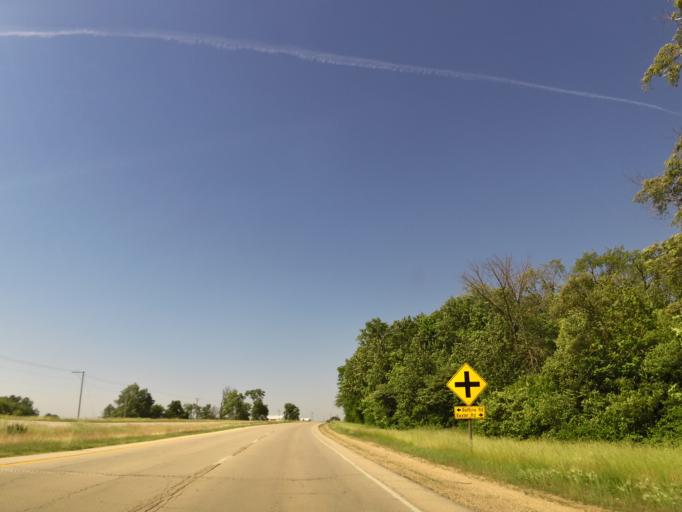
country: US
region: Illinois
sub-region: Ogle County
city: Davis Junction
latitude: 42.1638
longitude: -89.0756
